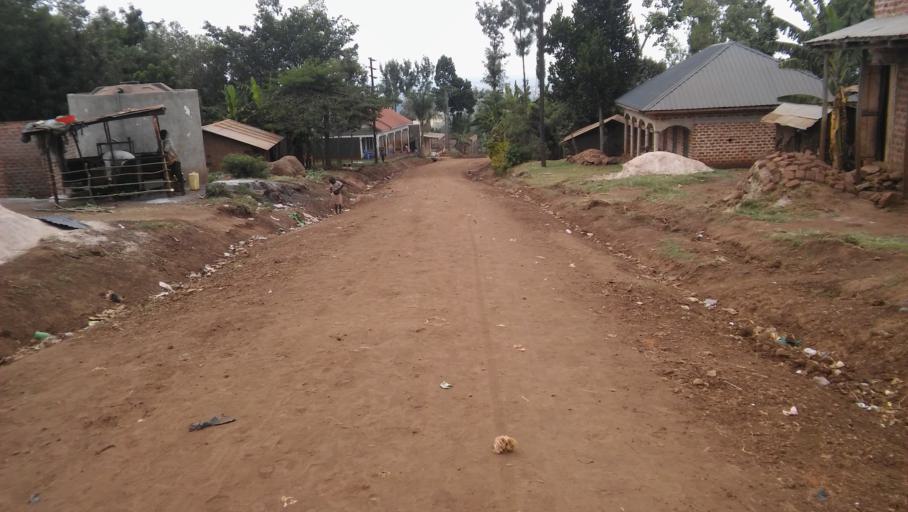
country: UG
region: Eastern Region
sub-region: Mbale District
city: Mbale
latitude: 1.0583
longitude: 34.2114
